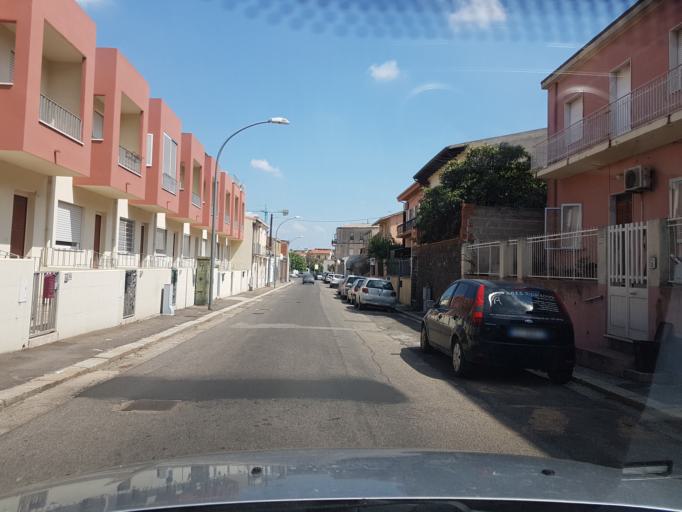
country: IT
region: Sardinia
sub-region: Provincia di Oristano
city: Oristano
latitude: 39.9055
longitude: 8.5994
